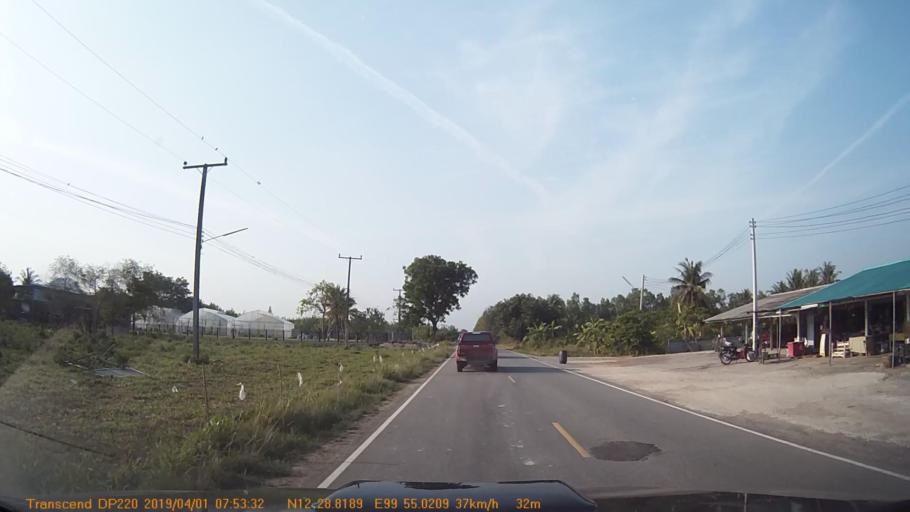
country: TH
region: Prachuap Khiri Khan
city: Pran Buri
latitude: 12.4801
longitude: 99.9170
